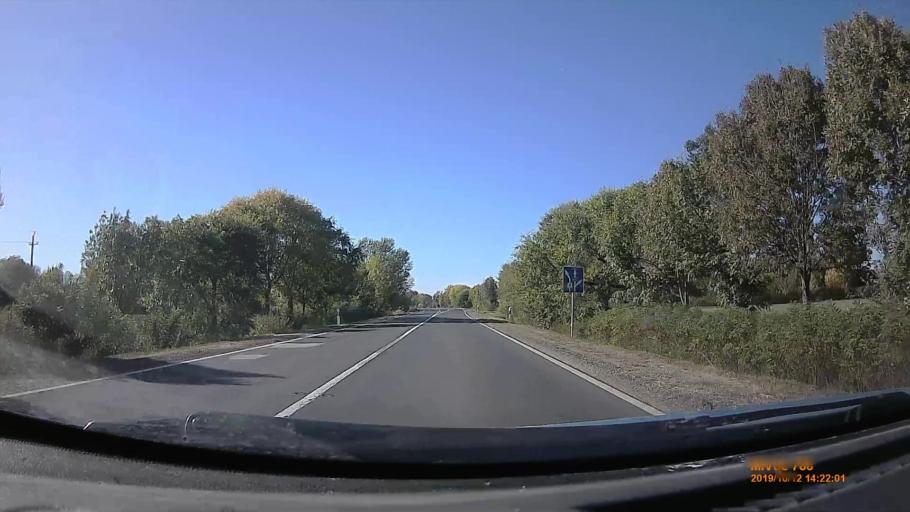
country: HU
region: Hajdu-Bihar
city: Biharkeresztes
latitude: 47.1414
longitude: 21.7228
